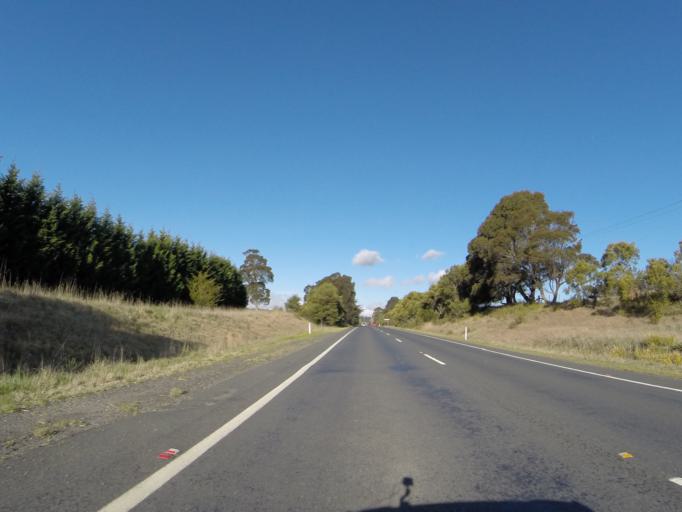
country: AU
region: New South Wales
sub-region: Wingecarribee
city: Moss Vale
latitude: -34.5722
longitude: 150.4583
